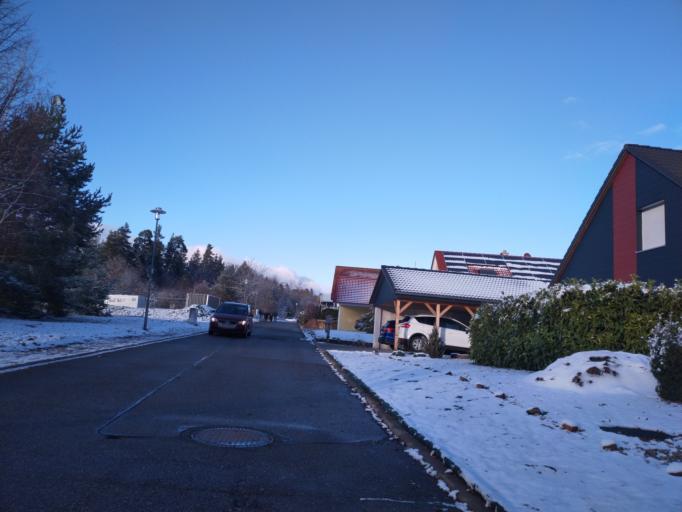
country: DE
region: Baden-Wuerttemberg
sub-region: Karlsruhe Region
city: Simmersfeld
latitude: 48.6226
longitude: 8.5069
